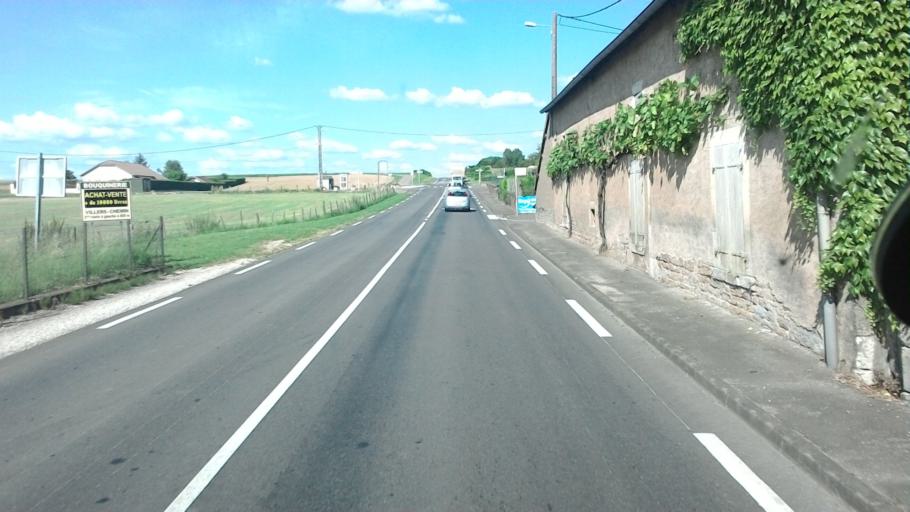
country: FR
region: Franche-Comte
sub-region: Departement de la Haute-Saone
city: Gy
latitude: 47.4305
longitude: 5.8589
